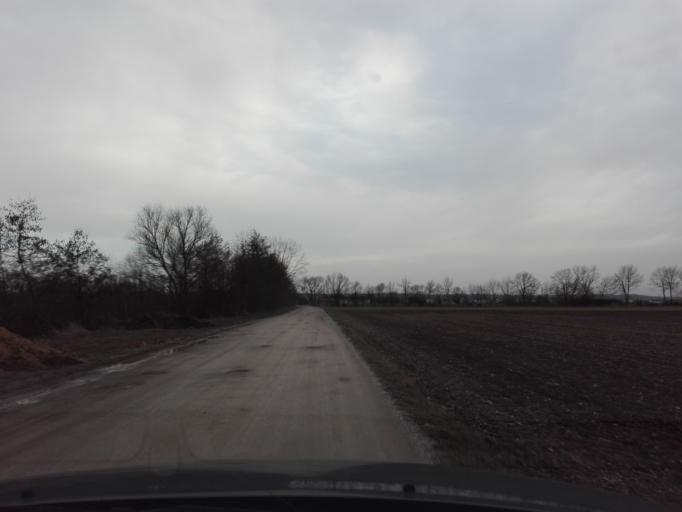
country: AT
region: Upper Austria
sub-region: Politischer Bezirk Linz-Land
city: Horsching
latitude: 48.2128
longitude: 14.1538
